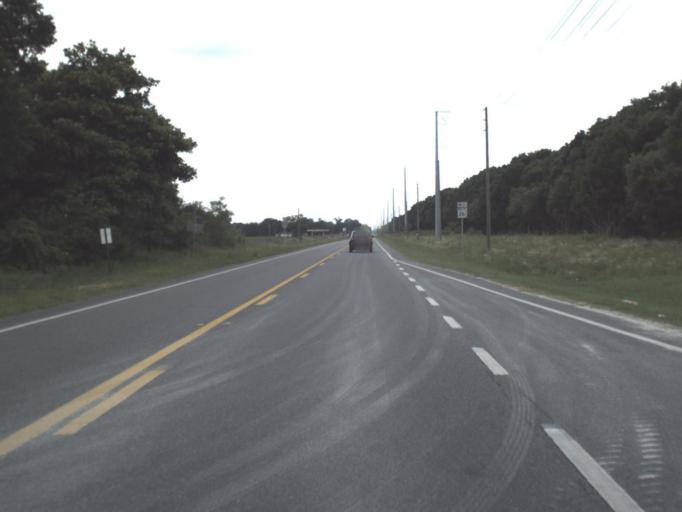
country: US
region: Florida
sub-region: Gilchrist County
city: Trenton
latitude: 29.6123
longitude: -82.8985
